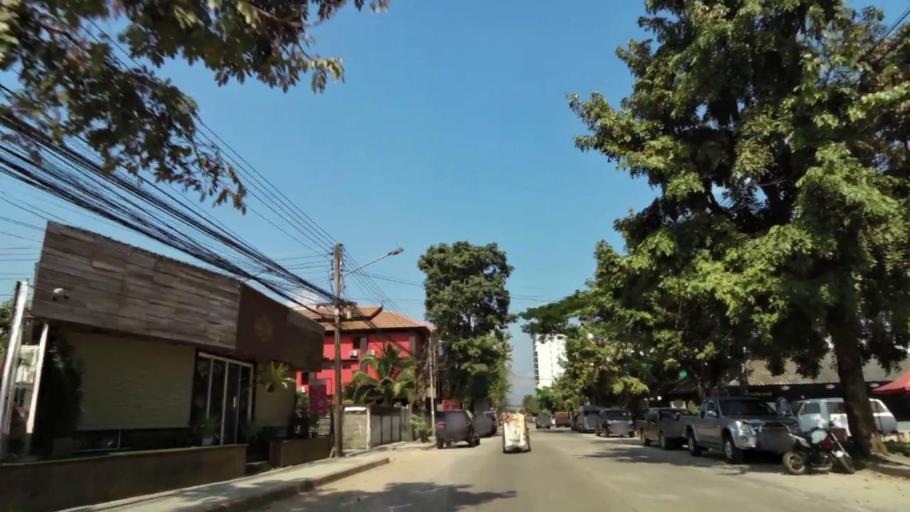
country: TH
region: Chiang Rai
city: Chiang Rai
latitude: 19.8974
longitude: 99.8277
